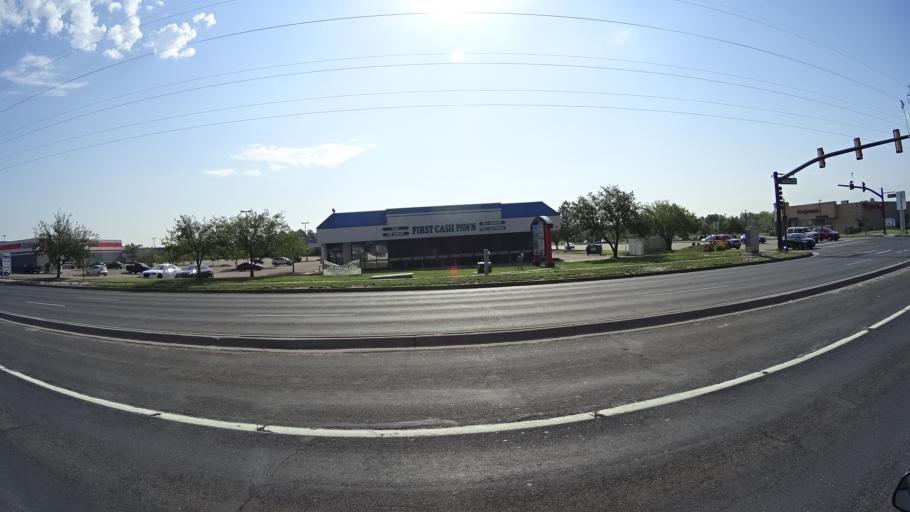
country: US
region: Colorado
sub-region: El Paso County
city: Stratmoor
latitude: 38.8052
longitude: -104.7577
